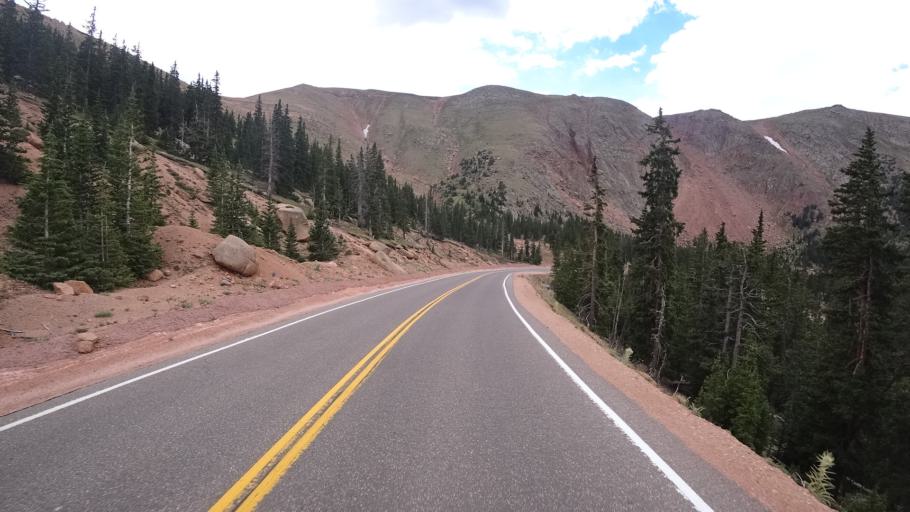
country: US
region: Colorado
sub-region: El Paso County
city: Cascade-Chipita Park
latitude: 38.8737
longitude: -105.0701
